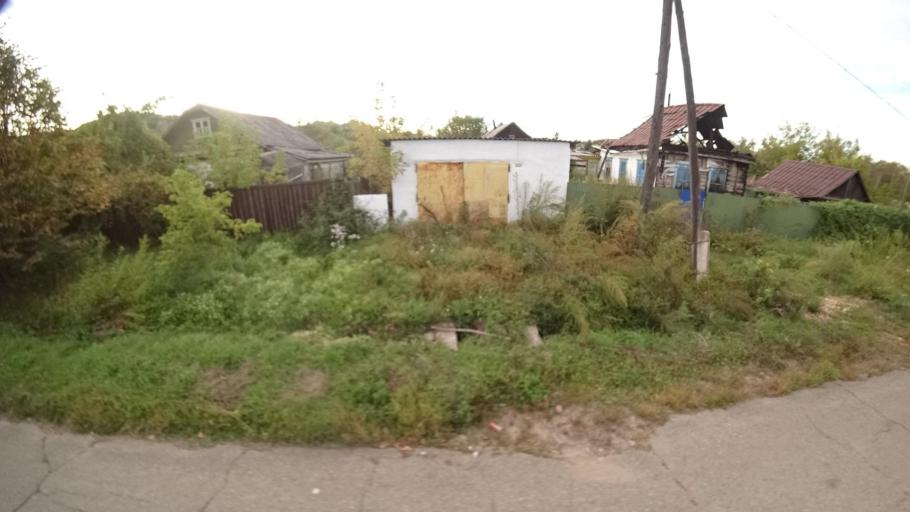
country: RU
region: Primorskiy
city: Yakovlevka
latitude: 44.4181
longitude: 133.4719
